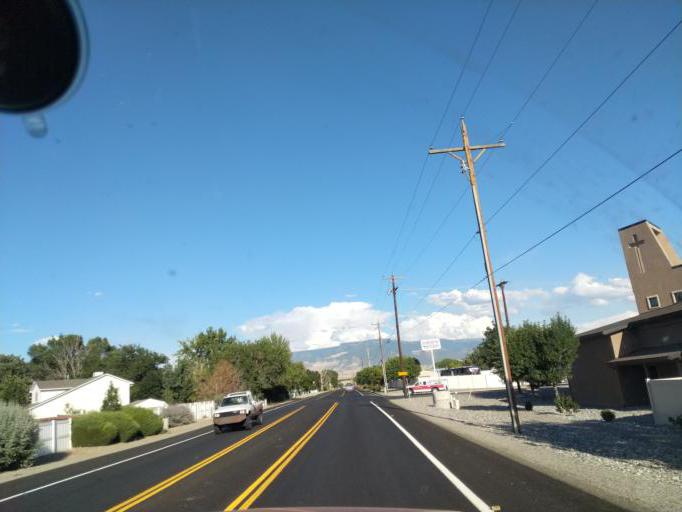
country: US
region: Colorado
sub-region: Mesa County
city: Clifton
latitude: 39.0629
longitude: -108.4672
